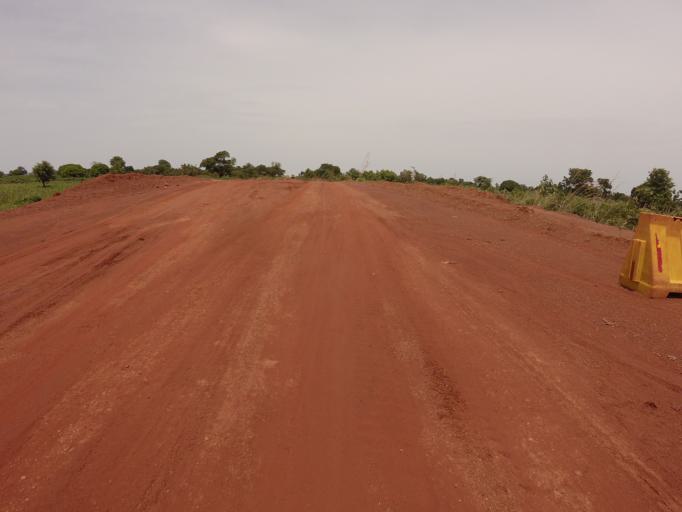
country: GH
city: Kpandae
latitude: 8.7879
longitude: 0.0578
